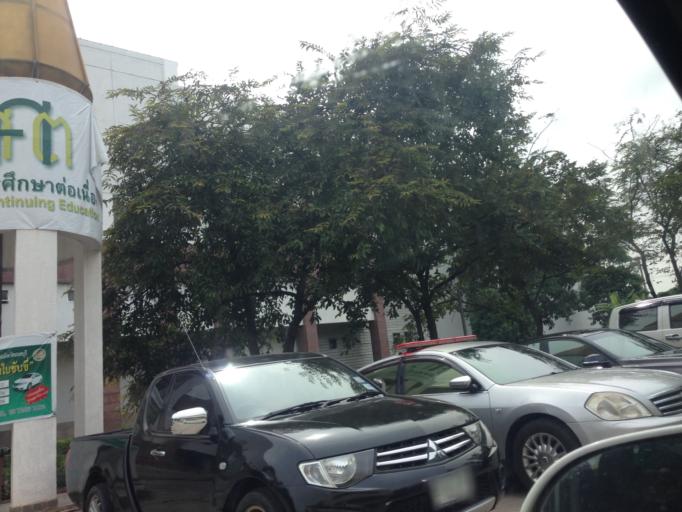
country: TH
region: Nonthaburi
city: Pak Kret
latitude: 13.9094
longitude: 100.5357
